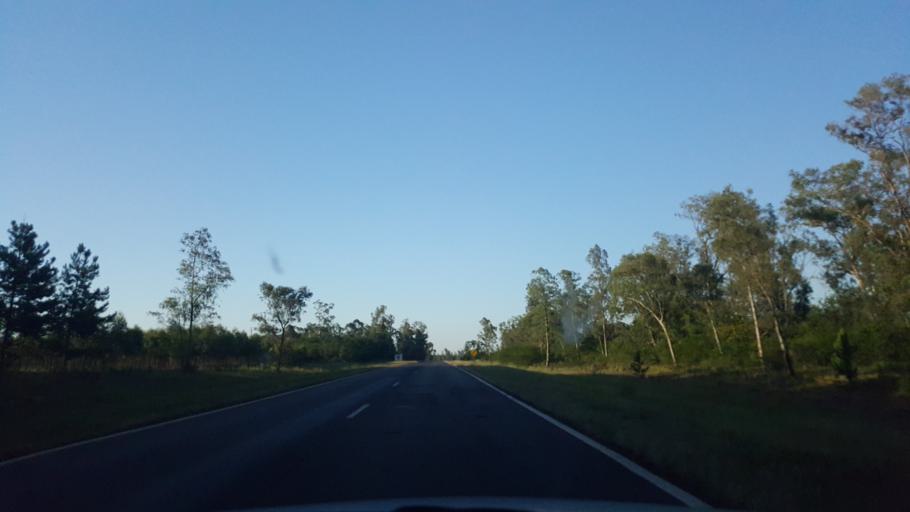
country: AR
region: Corrientes
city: Santo Tome
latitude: -28.4929
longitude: -56.1141
